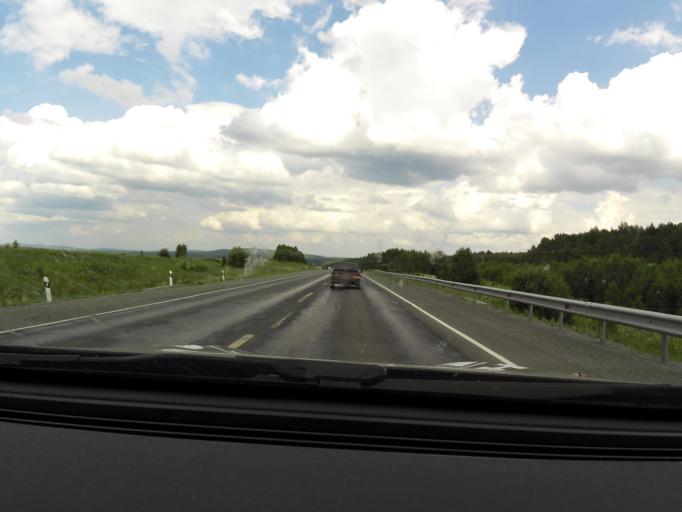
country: RU
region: Sverdlovsk
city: Bisert'
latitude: 56.8148
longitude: 58.7459
